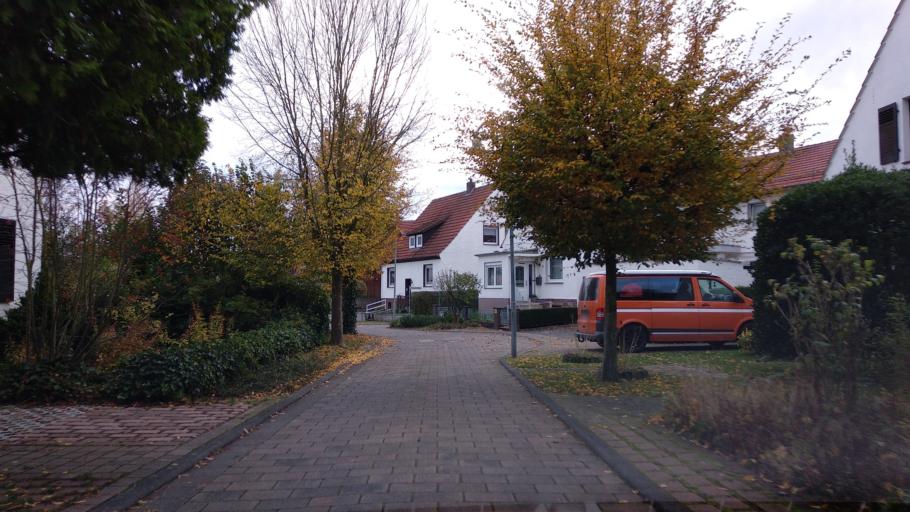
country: DE
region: North Rhine-Westphalia
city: Beverungen
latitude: 51.6636
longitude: 9.3671
